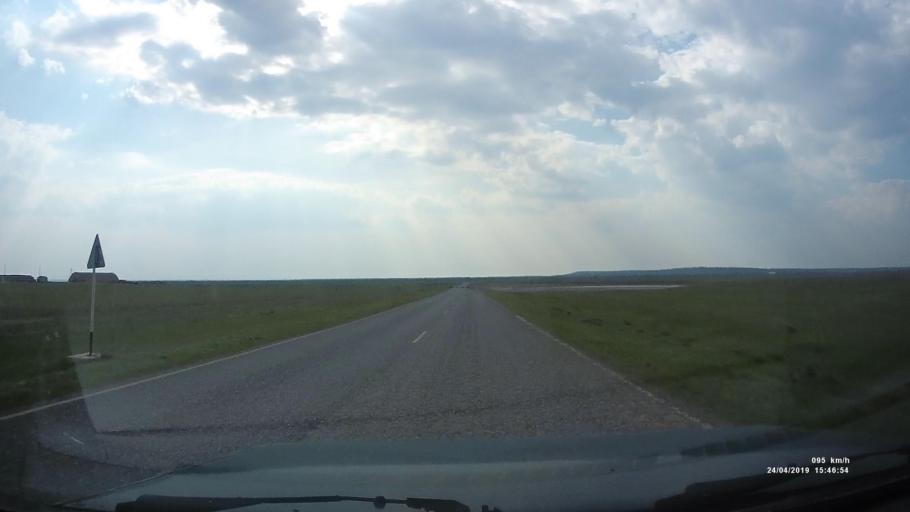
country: RU
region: Kalmykiya
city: Yashalta
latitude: 46.5935
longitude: 42.7042
